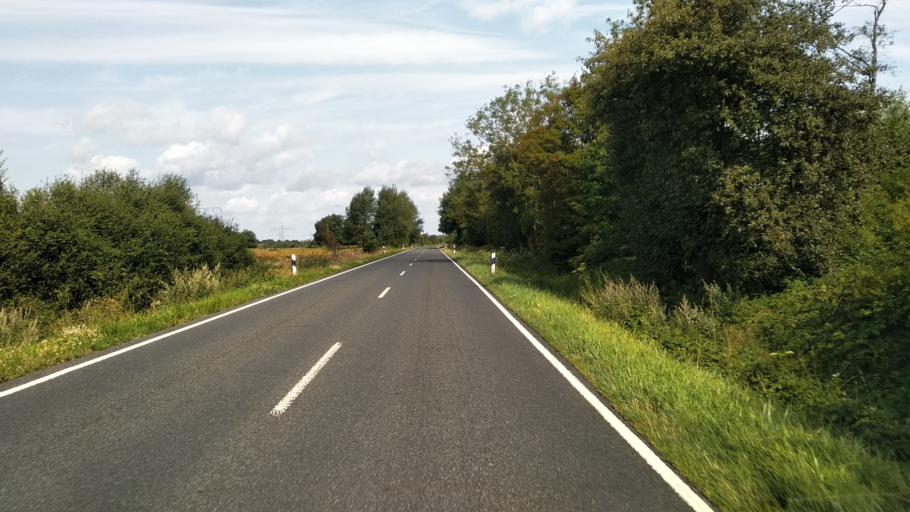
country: DE
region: Schleswig-Holstein
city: Lottorf
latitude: 54.4451
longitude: 9.5955
